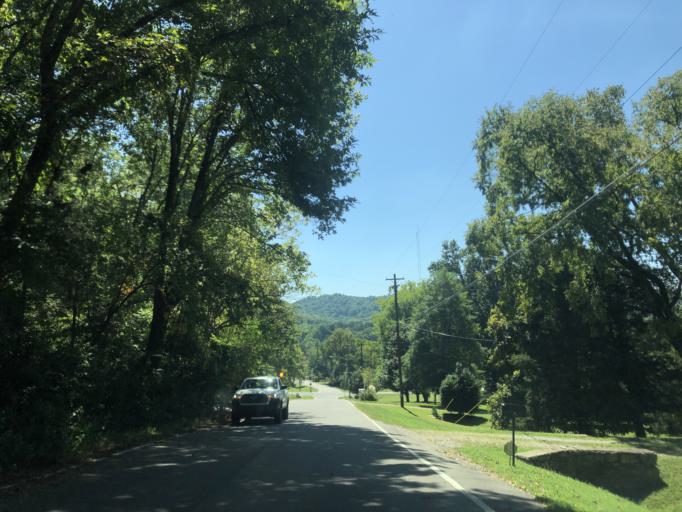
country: US
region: Tennessee
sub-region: Davidson County
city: Forest Hills
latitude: 36.0668
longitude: -86.8358
